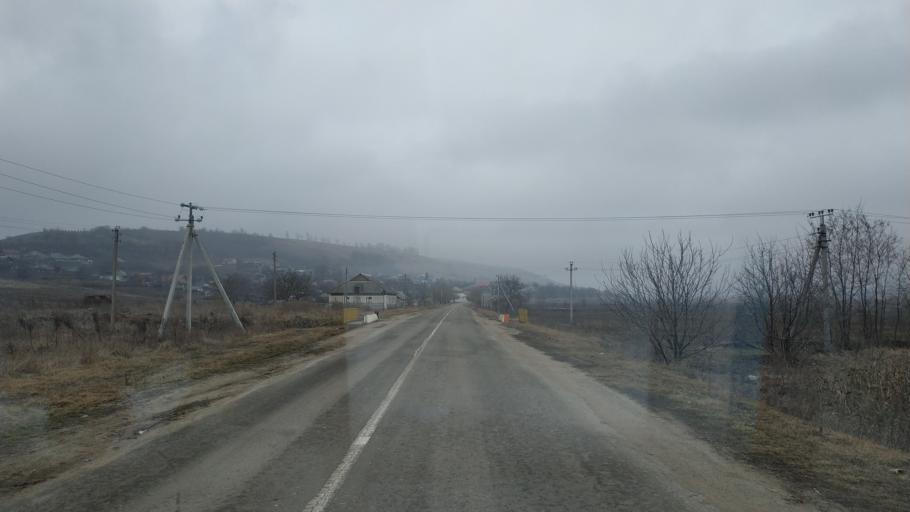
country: MD
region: Hincesti
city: Hincesti
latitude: 46.9561
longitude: 28.4921
